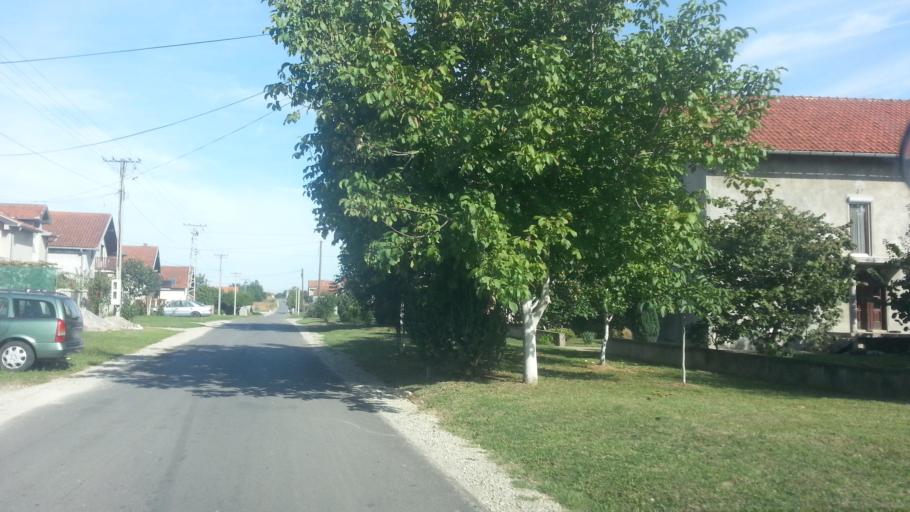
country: RS
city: Novi Banovci
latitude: 44.9697
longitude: 20.2761
